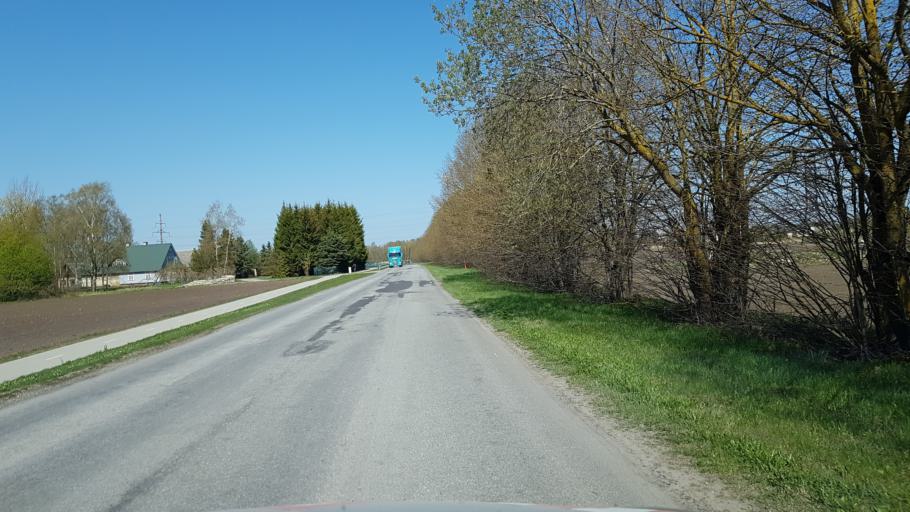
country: EE
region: Harju
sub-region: Joelaehtme vald
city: Loo
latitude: 59.4213
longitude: 24.9437
